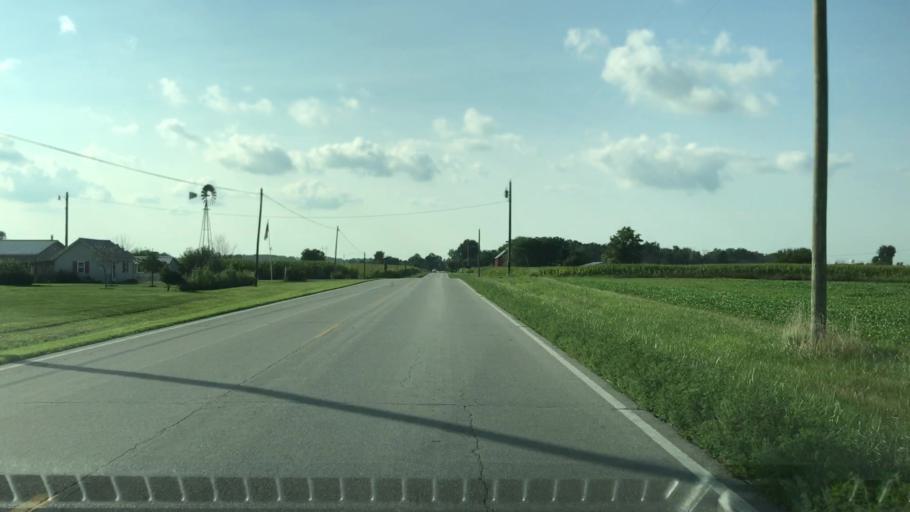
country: US
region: Ohio
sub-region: Union County
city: Marysville
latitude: 40.2016
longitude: -83.3459
